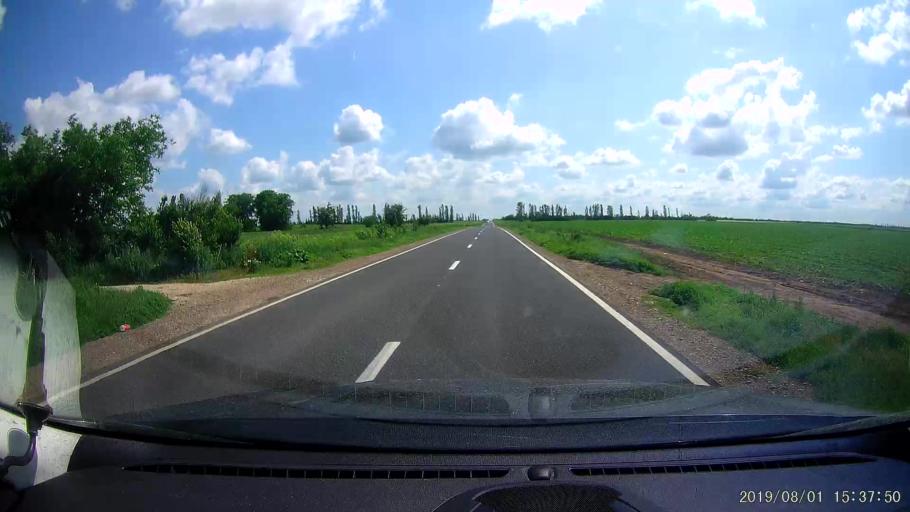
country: RO
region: Braila
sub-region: Comuna Insuratei
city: Insuratei
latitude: 44.8958
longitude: 27.5847
